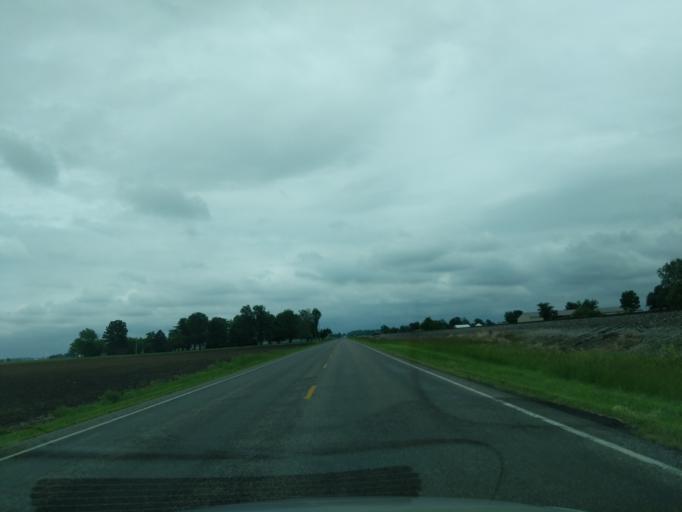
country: US
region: Indiana
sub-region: Madison County
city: Elwood
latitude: 40.2792
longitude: -85.9035
